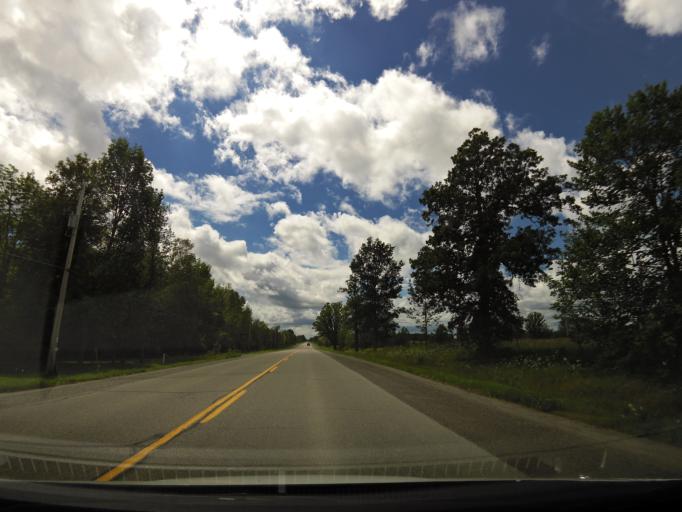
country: CA
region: Ontario
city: Carleton Place
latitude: 45.0634
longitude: -76.0378
